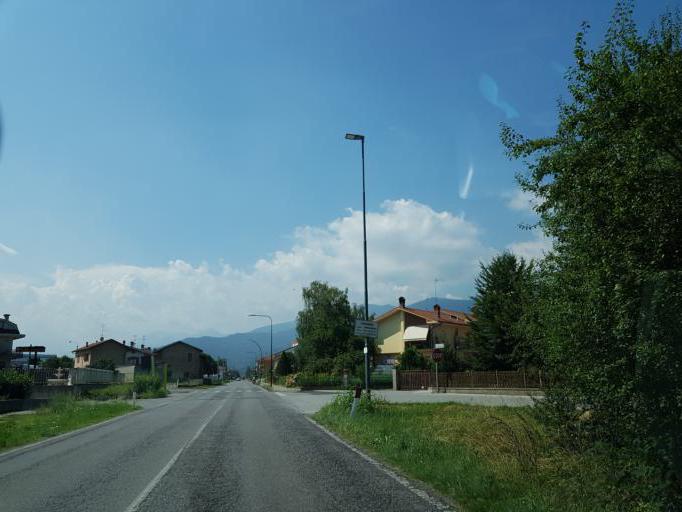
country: IT
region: Piedmont
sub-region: Provincia di Cuneo
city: Montemale di Cuneo
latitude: 44.4556
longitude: 7.3826
